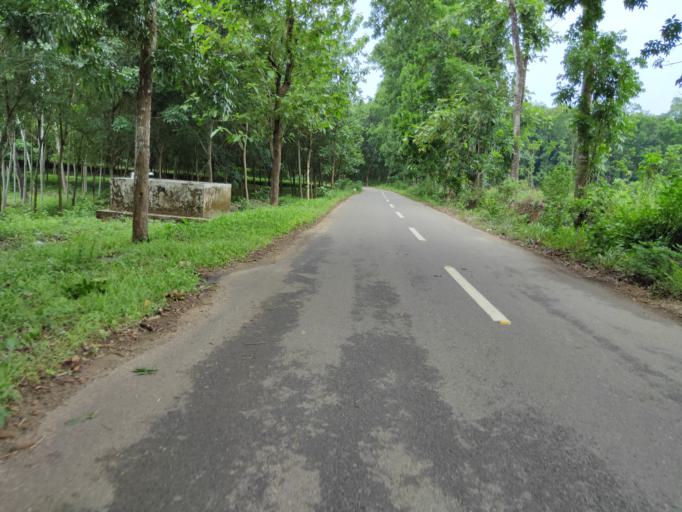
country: IN
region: Kerala
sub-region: Malappuram
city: Manjeri
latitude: 11.2306
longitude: 76.2498
